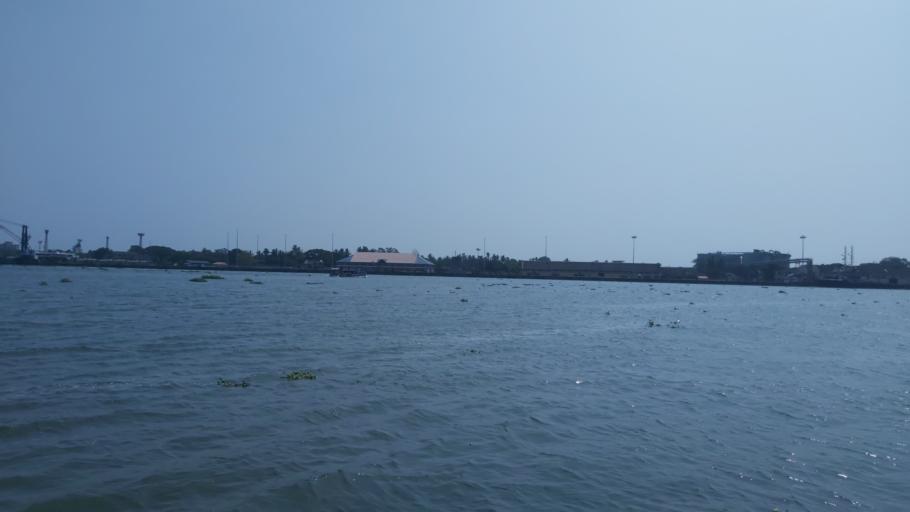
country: IN
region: Kerala
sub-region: Ernakulam
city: Cochin
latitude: 9.9711
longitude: 76.2692
